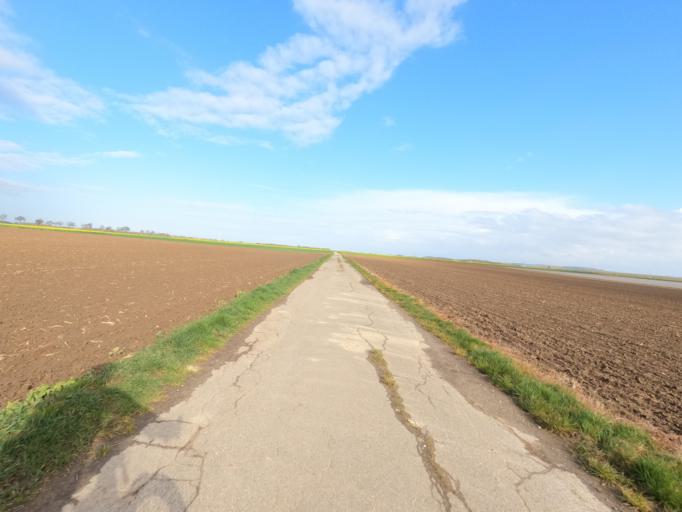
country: DE
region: North Rhine-Westphalia
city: Huckelhoven
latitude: 51.0012
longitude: 6.2106
